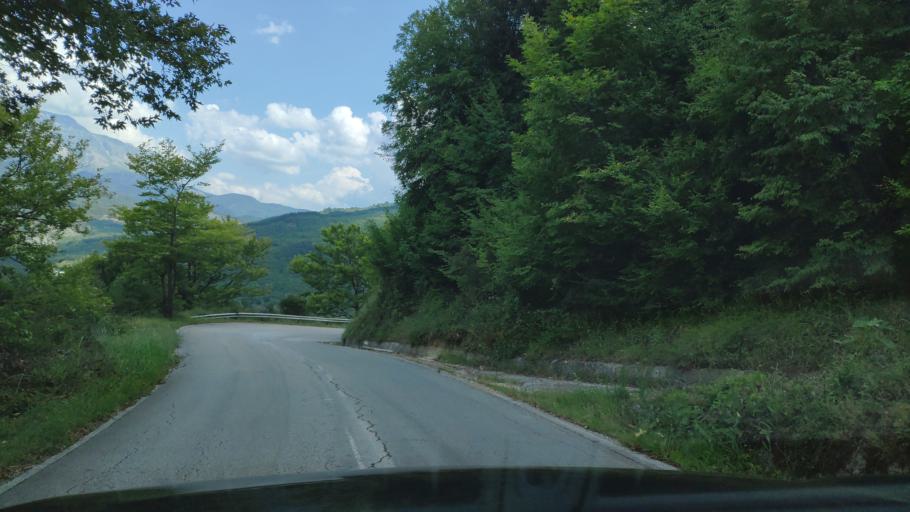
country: GR
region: Epirus
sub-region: Nomos Artas
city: Agios Dimitrios
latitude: 39.4570
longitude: 21.0293
